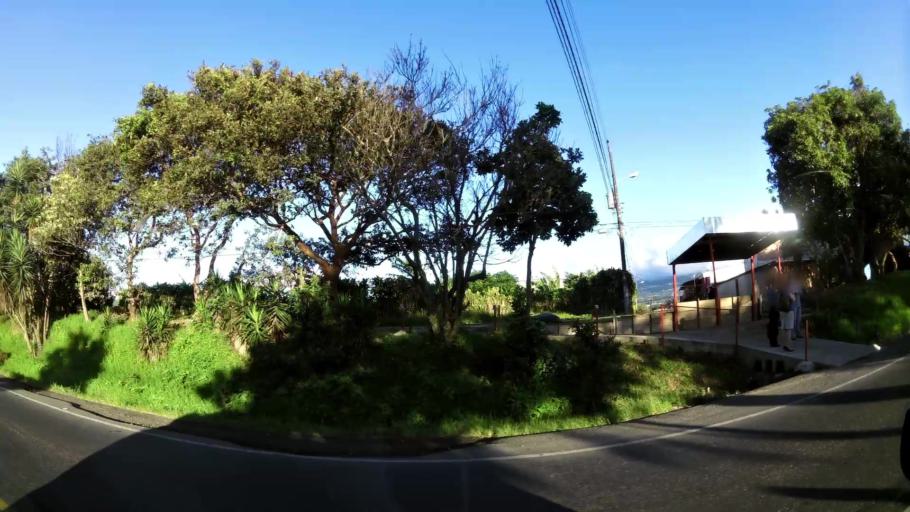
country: CR
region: Heredia
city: Angeles
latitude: 9.9901
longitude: -84.0415
